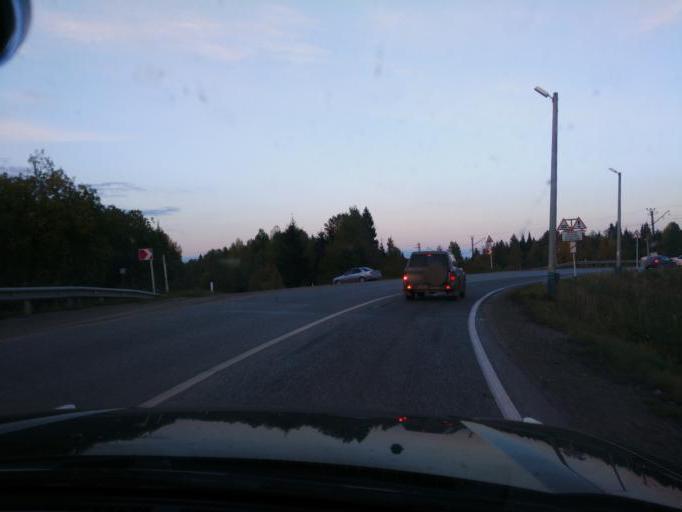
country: RU
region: Perm
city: Polazna
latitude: 58.3041
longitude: 56.6225
